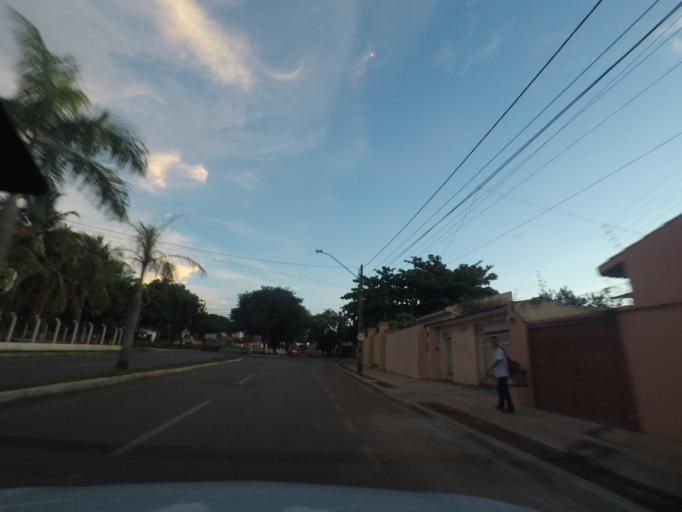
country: BR
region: Goias
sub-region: Goiania
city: Goiania
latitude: -16.6991
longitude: -49.3116
